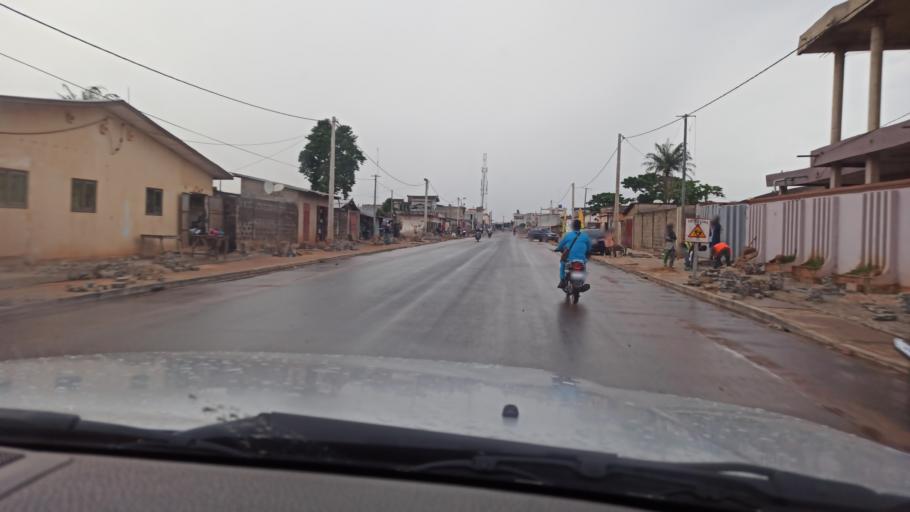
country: BJ
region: Queme
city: Porto-Novo
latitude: 6.4954
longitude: 2.6422
